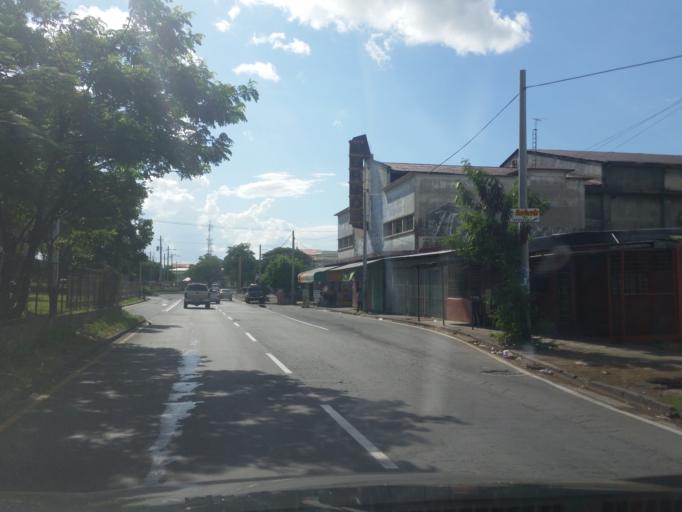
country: NI
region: Managua
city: Managua
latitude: 12.1545
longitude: -86.2686
